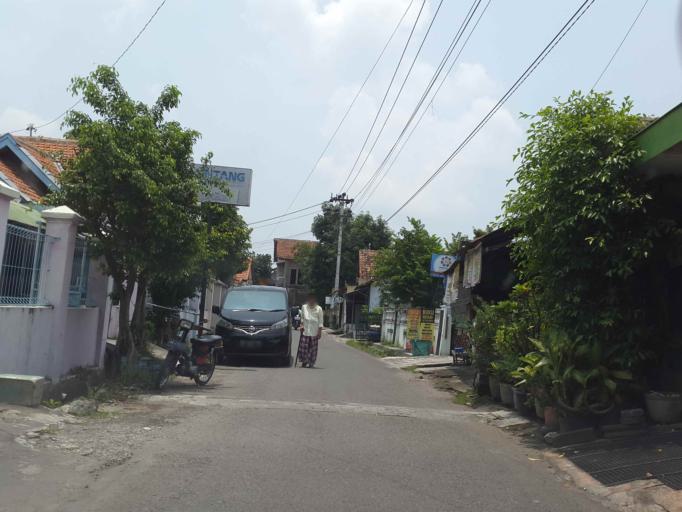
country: ID
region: Central Java
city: Colomadu
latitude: -7.5577
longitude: 110.7825
